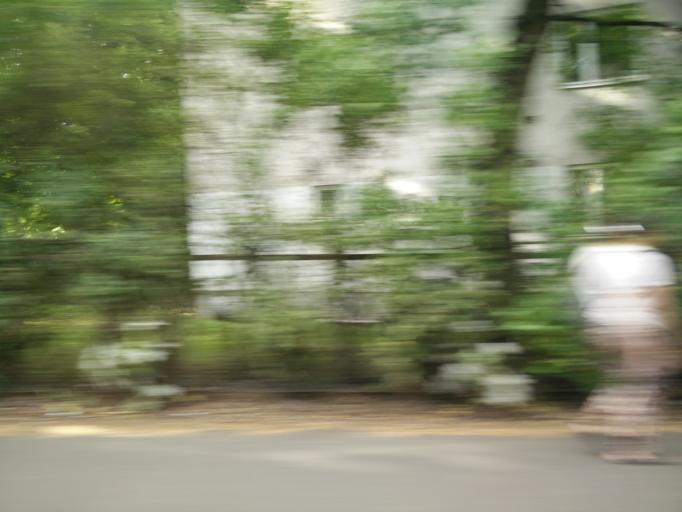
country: NO
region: Oslo
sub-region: Oslo
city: Oslo
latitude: 59.9356
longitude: 10.7387
